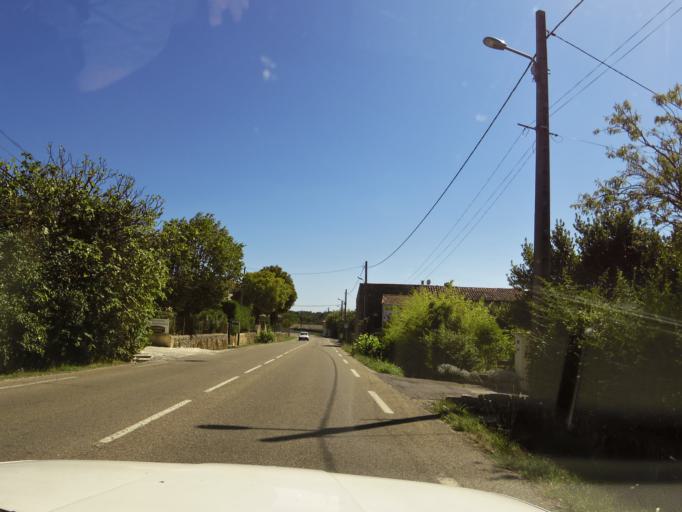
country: FR
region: Languedoc-Roussillon
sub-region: Departement du Gard
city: Vezenobres
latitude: 44.0543
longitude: 4.1306
